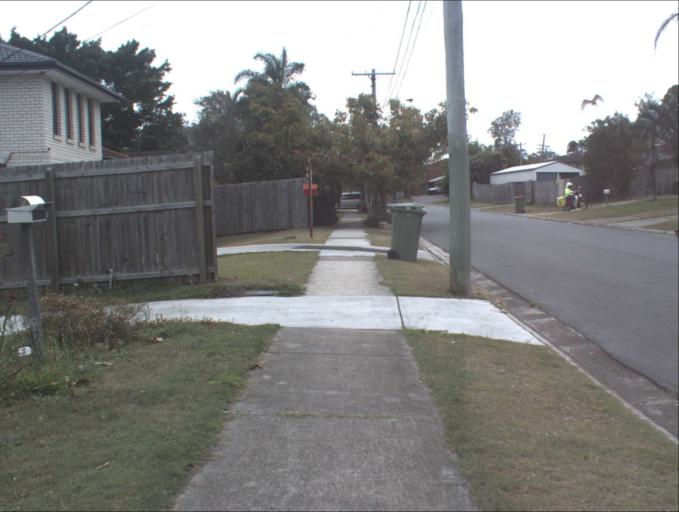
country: AU
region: Queensland
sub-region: Logan
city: Logan City
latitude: -27.6287
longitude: 153.1209
